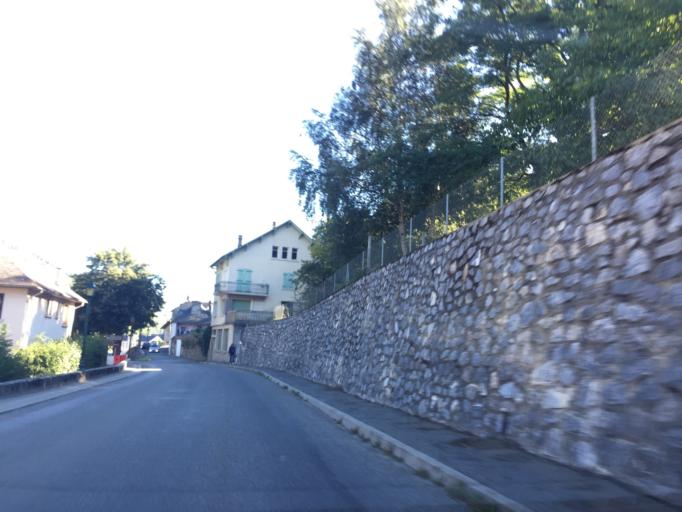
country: FR
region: Midi-Pyrenees
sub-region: Departement des Hautes-Pyrenees
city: Saint-Lary-Soulan
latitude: 42.9021
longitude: 0.3581
